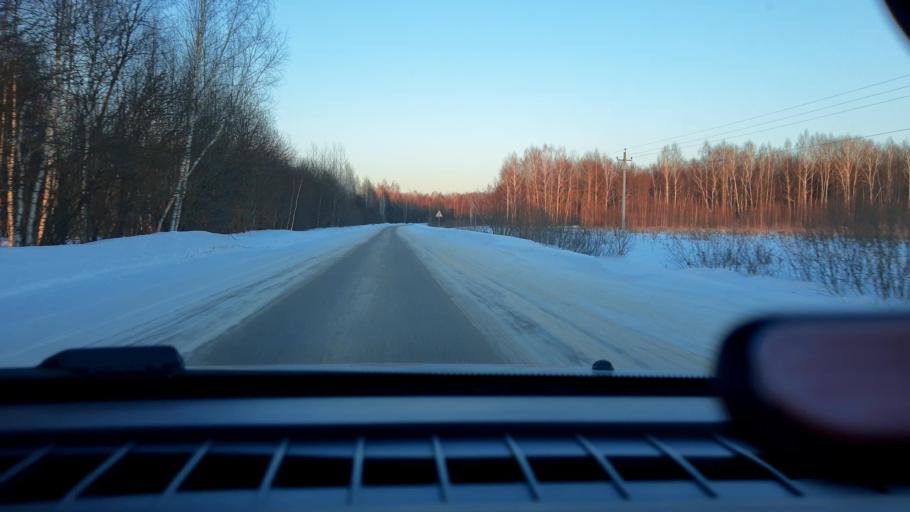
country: RU
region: Nizjnij Novgorod
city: Lyskovo
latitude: 56.1345
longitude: 45.0036
